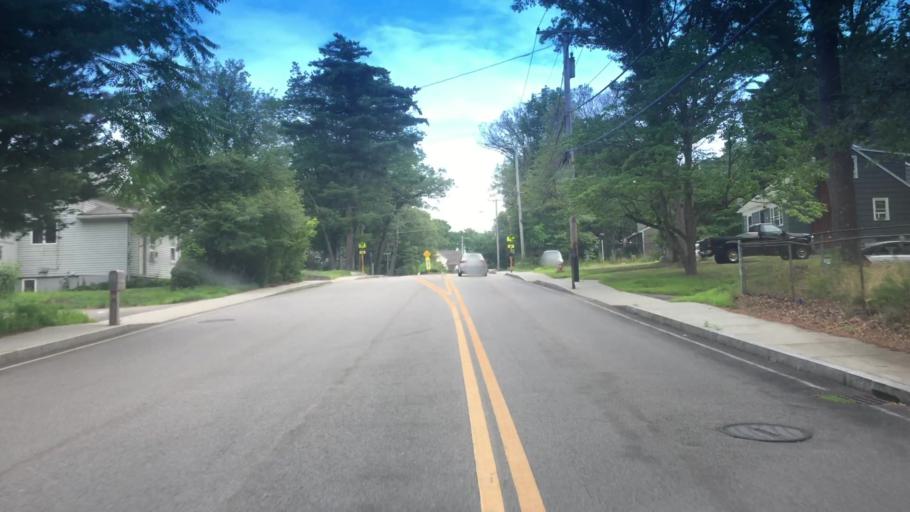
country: US
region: Massachusetts
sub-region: Norfolk County
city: Franklin
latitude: 42.1093
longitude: -71.3951
